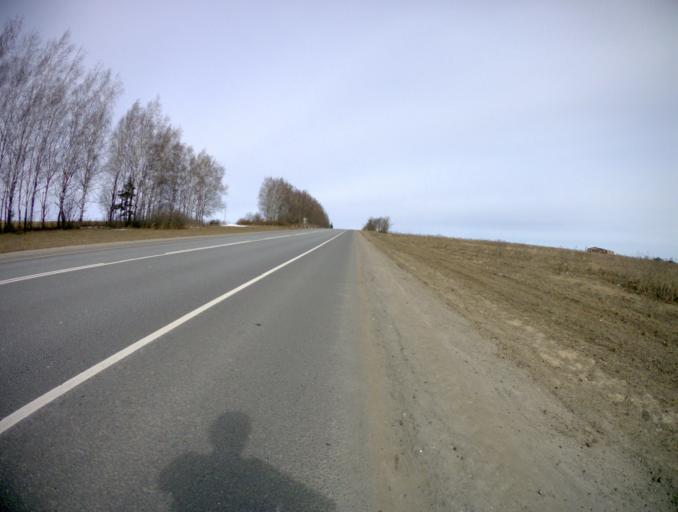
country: RU
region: Vladimir
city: Bogolyubovo
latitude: 56.2695
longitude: 40.4652
